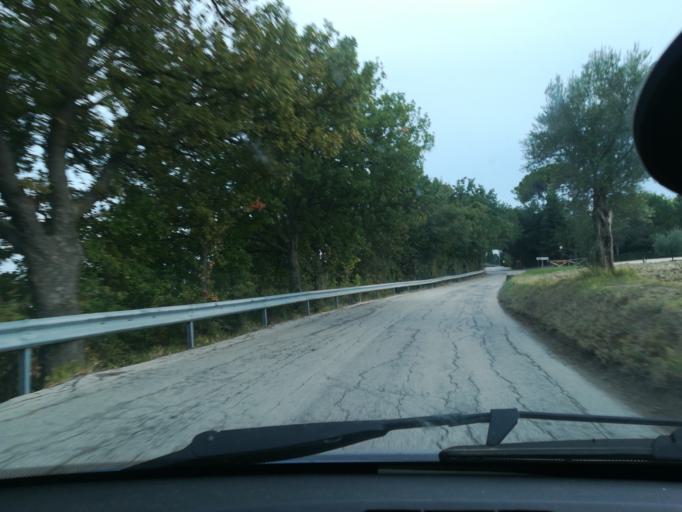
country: IT
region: The Marches
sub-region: Provincia di Macerata
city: Piediripa
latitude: 43.2916
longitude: 13.4885
